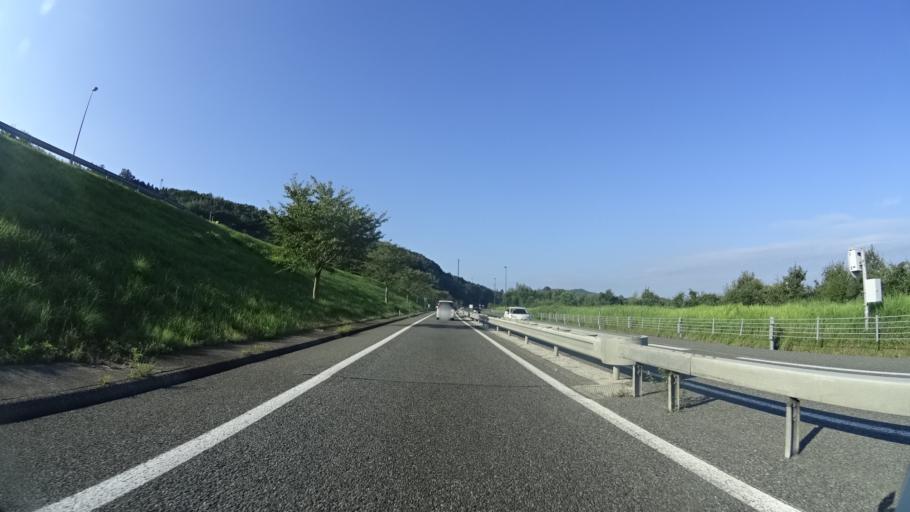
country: JP
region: Shimane
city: Matsue-shi
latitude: 35.4275
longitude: 133.0179
